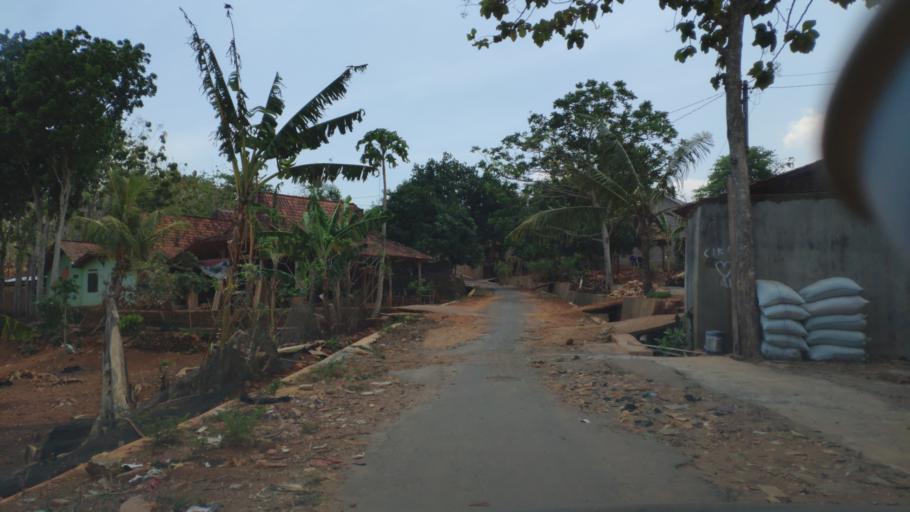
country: ID
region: Central Java
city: Guyangan
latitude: -6.9195
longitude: 111.1232
